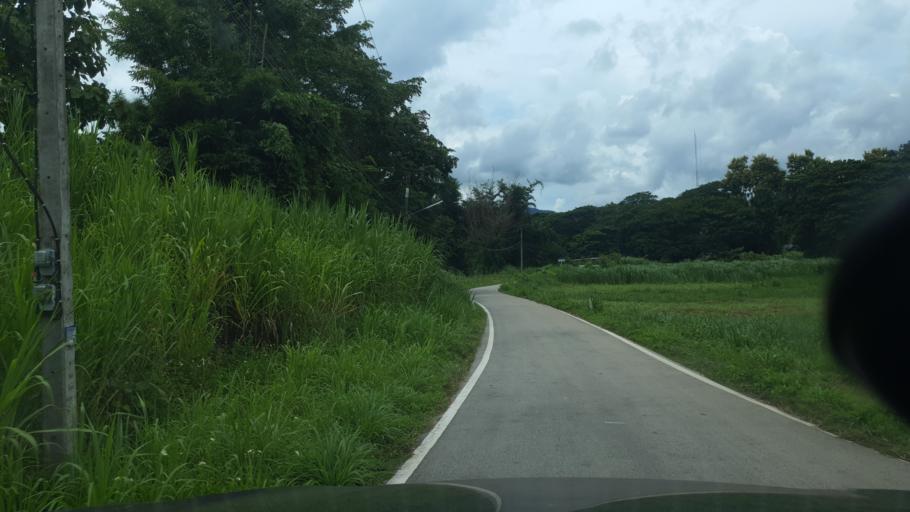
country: TH
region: Lampang
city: Hang Chat
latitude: 18.4017
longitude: 99.2629
